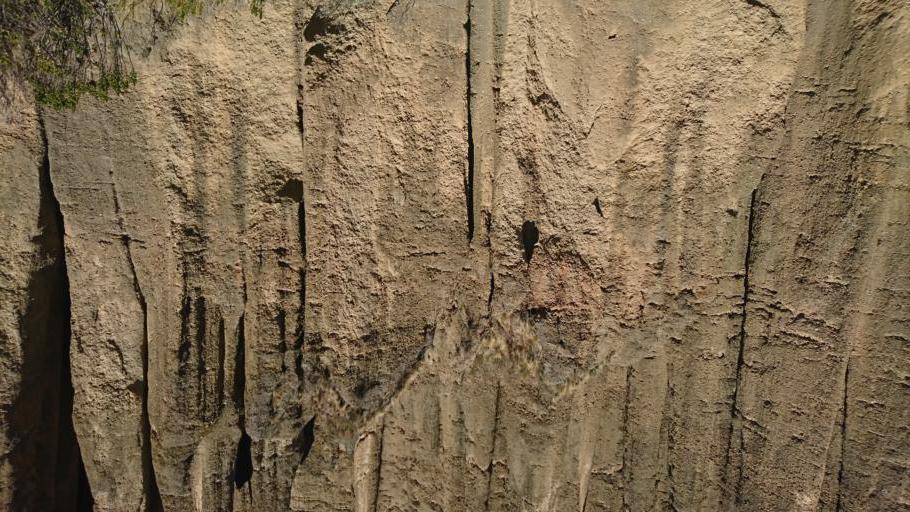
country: BO
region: La Paz
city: La Paz
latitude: -16.5396
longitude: -68.0056
